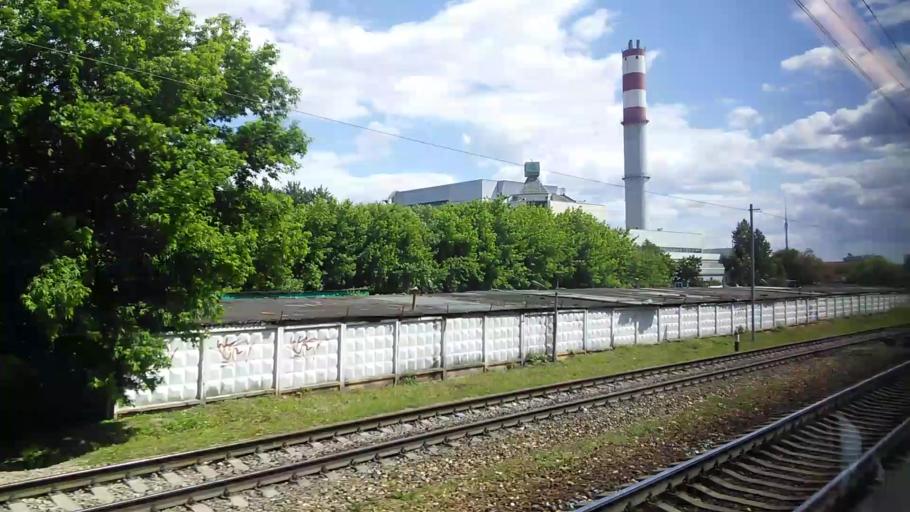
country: RU
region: Moscow
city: Slobodka
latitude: 55.8630
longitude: 37.5743
